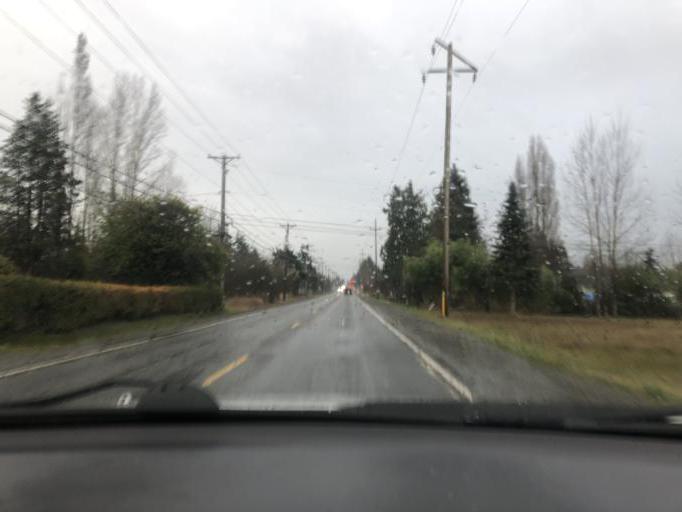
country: US
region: Washington
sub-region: Pierce County
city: Waller
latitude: 47.1957
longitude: -122.3891
